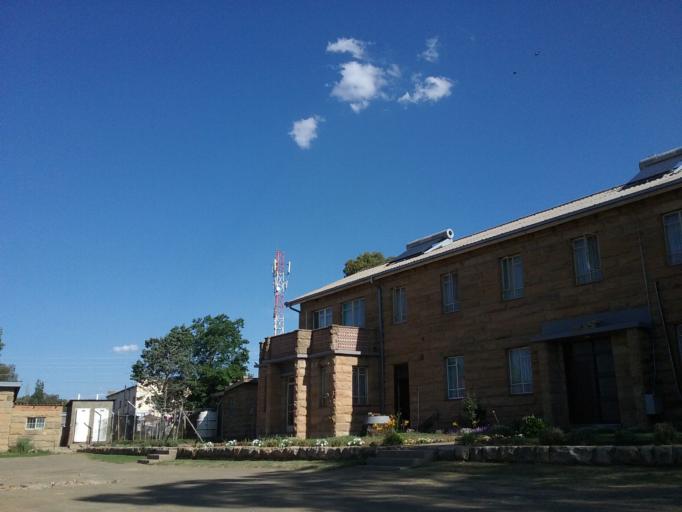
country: LS
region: Maseru
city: Maseru
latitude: -29.3170
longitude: 27.4957
